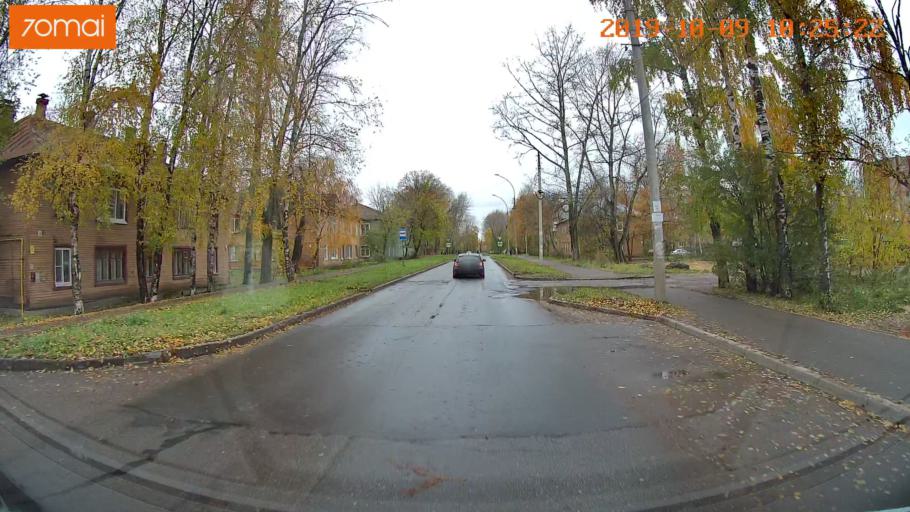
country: RU
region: Vologda
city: Vologda
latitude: 59.2131
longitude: 39.9293
